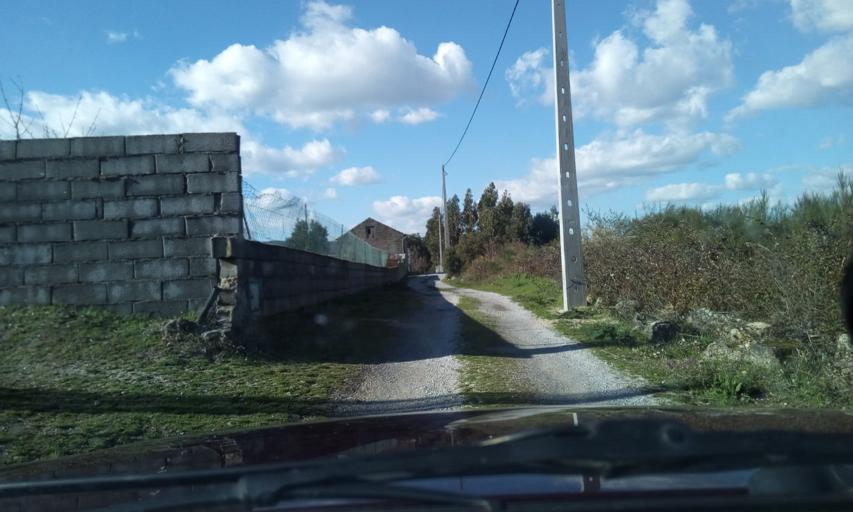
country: PT
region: Guarda
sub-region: Fornos de Algodres
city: Fornos de Algodres
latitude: 40.6111
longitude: -7.5043
